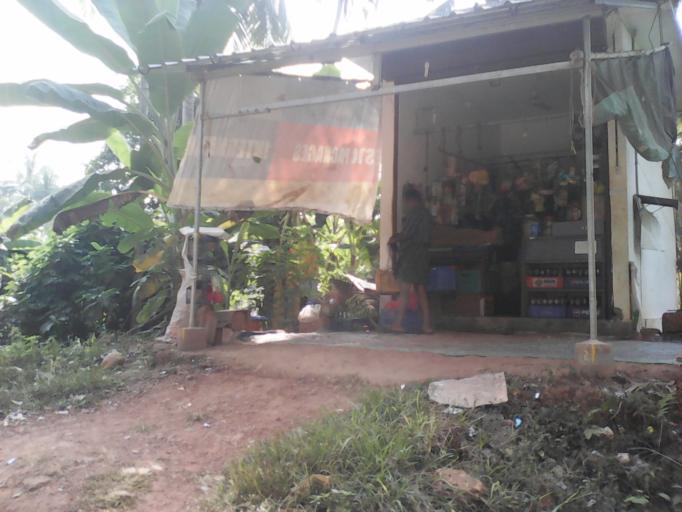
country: IN
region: Kerala
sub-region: Kozhikode
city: Kozhikode
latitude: 11.2801
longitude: 75.8160
